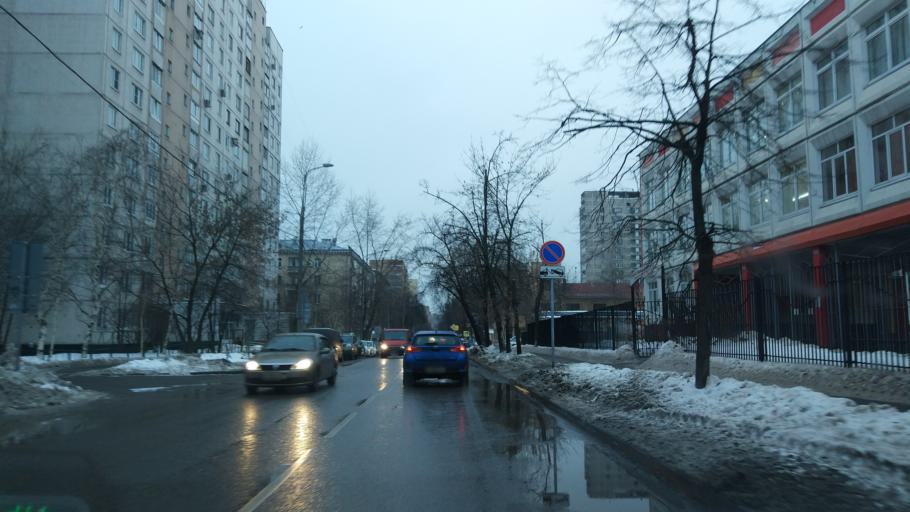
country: RU
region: Moskovskaya
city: Izmaylovo
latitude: 55.7913
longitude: 37.8123
